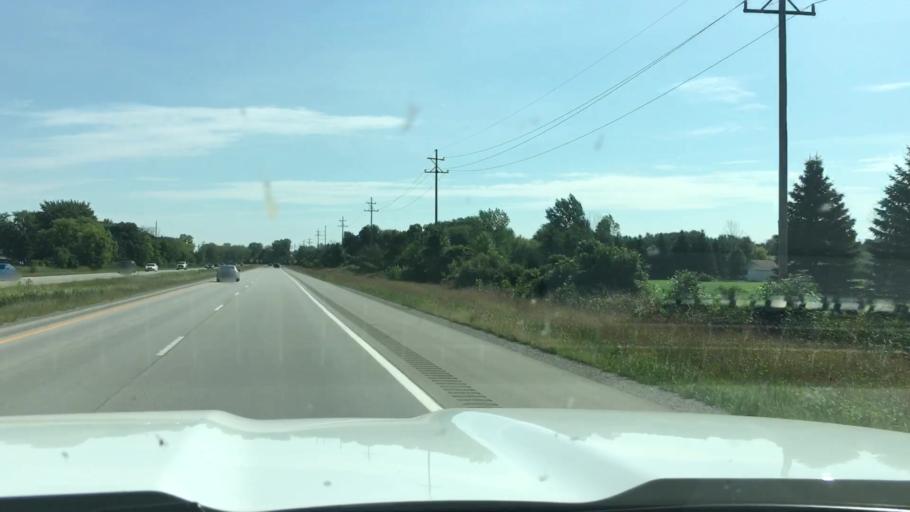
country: US
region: Michigan
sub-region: Bay County
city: Bay City
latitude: 43.5964
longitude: -83.9374
